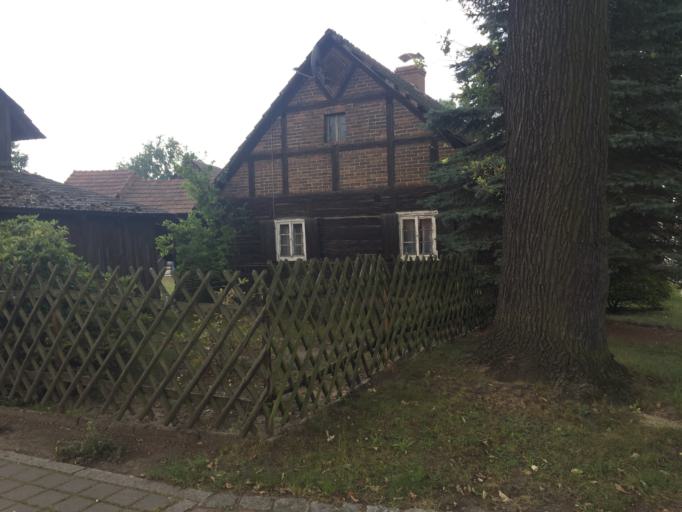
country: DE
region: Saxony
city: Schleife
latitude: 51.4911
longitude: 14.5130
